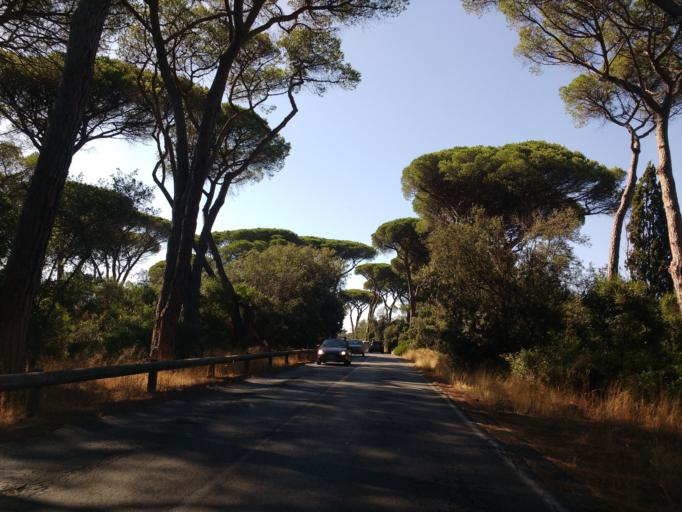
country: IT
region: Latium
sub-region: Citta metropolitana di Roma Capitale
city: Acilia-Castel Fusano-Ostia Antica
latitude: 41.7242
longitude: 12.3438
